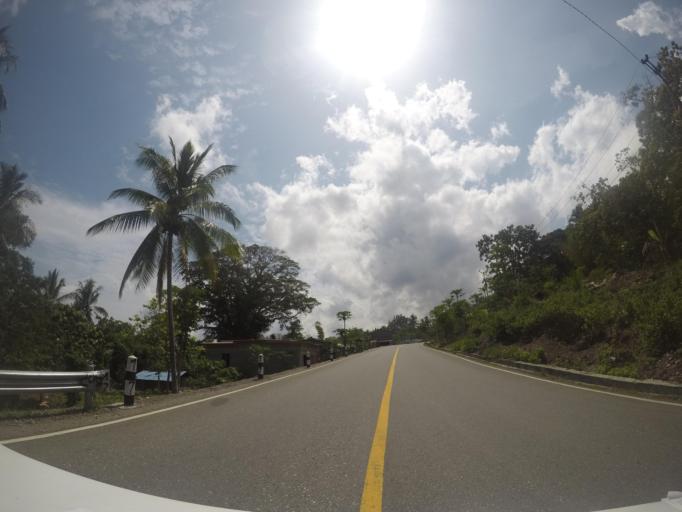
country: TL
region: Baucau
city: Baucau
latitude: -8.4859
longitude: 126.3435
